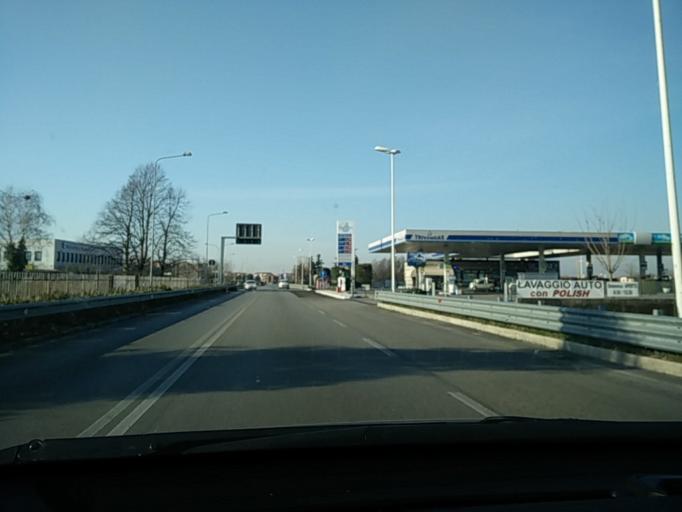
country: IT
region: Veneto
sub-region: Provincia di Venezia
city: San Dona di Piave
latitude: 45.6424
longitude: 12.5926
